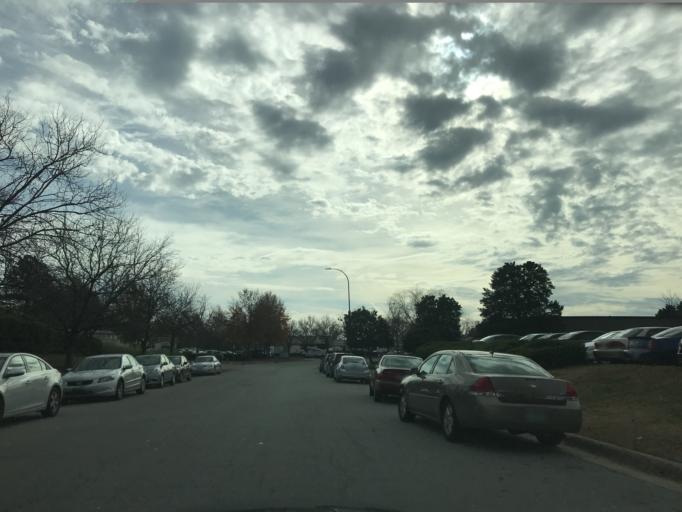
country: US
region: North Carolina
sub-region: Wake County
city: Raleigh
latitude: 35.8528
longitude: -78.5845
